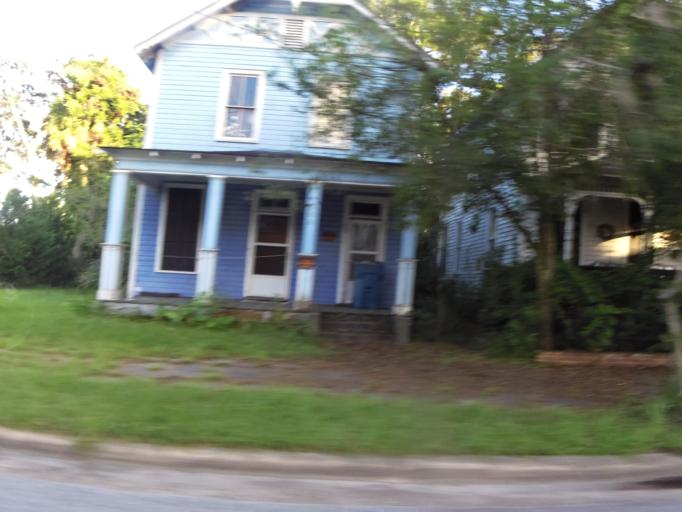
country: US
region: Georgia
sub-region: Glynn County
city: Brunswick
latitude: 31.1526
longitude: -81.4934
